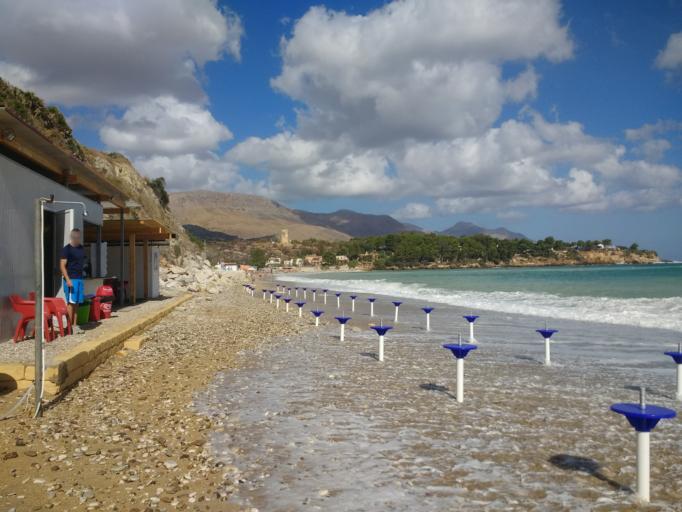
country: IT
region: Sicily
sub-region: Trapani
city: Castellammare del Golfo
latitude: 38.0552
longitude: 12.8432
